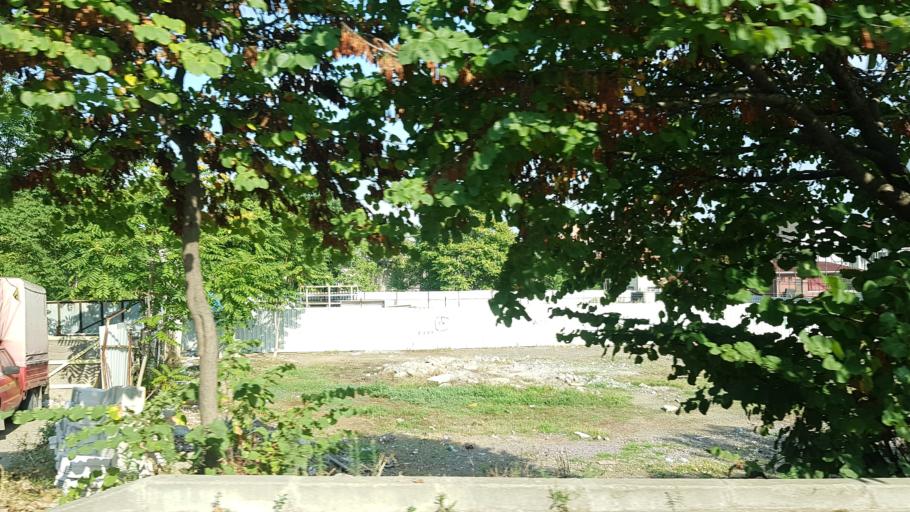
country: TR
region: Istanbul
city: Maltepe
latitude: 40.9014
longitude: 29.1961
